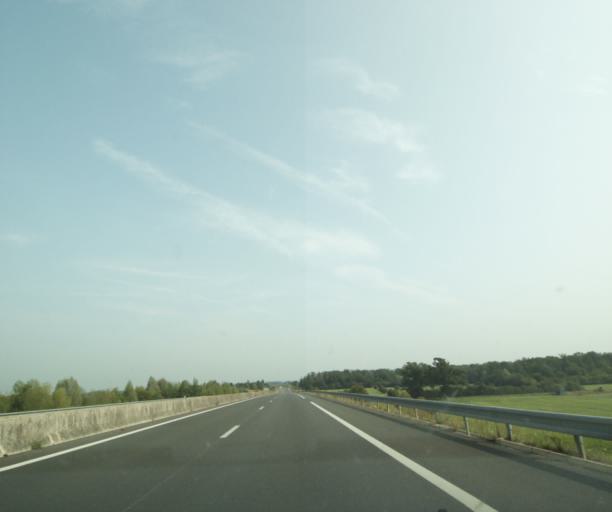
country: FR
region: Pays de la Loire
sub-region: Departement de la Sarthe
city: Beaumont-sur-Sarthe
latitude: 48.2043
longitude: 0.1752
